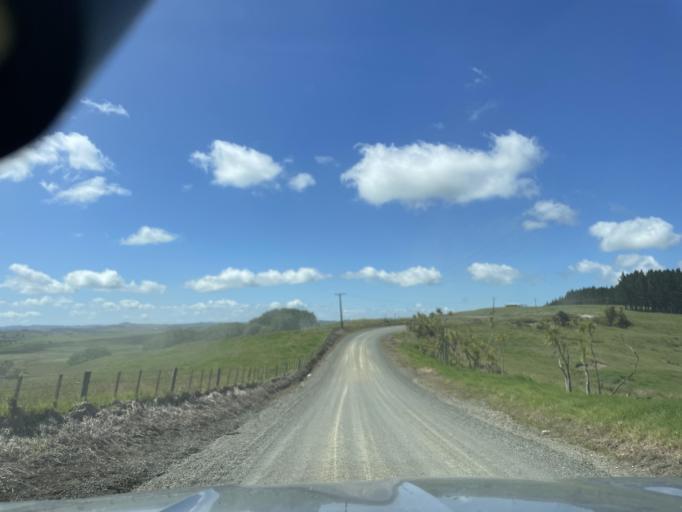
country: NZ
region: Auckland
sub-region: Auckland
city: Wellsford
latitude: -36.2446
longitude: 174.3645
